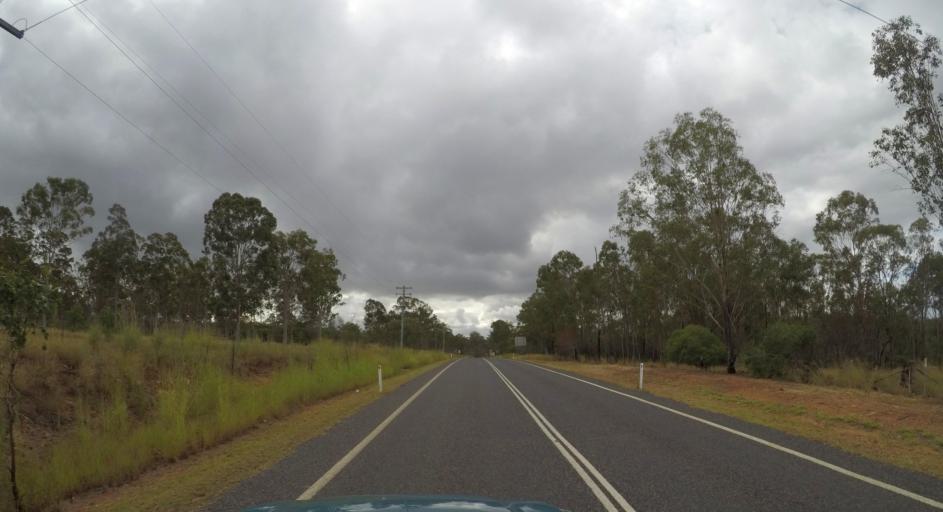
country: AU
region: Queensland
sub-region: North Burnett
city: Gayndah
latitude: -25.3617
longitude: 151.1195
